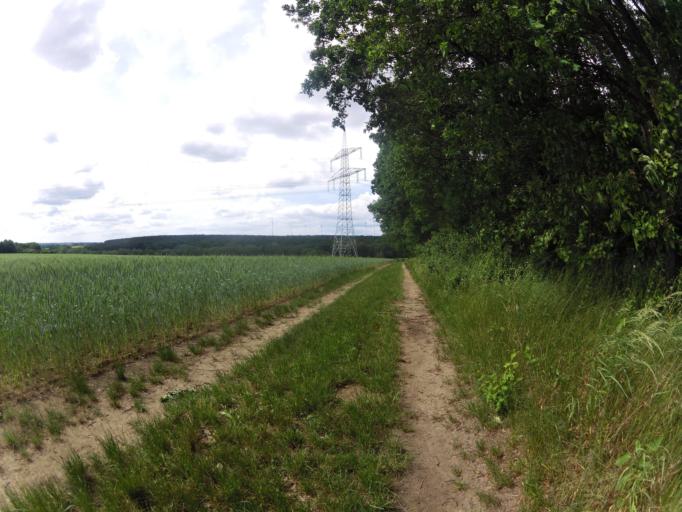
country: DE
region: Bavaria
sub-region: Regierungsbezirk Unterfranken
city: Ochsenfurt
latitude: 49.6961
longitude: 10.0697
